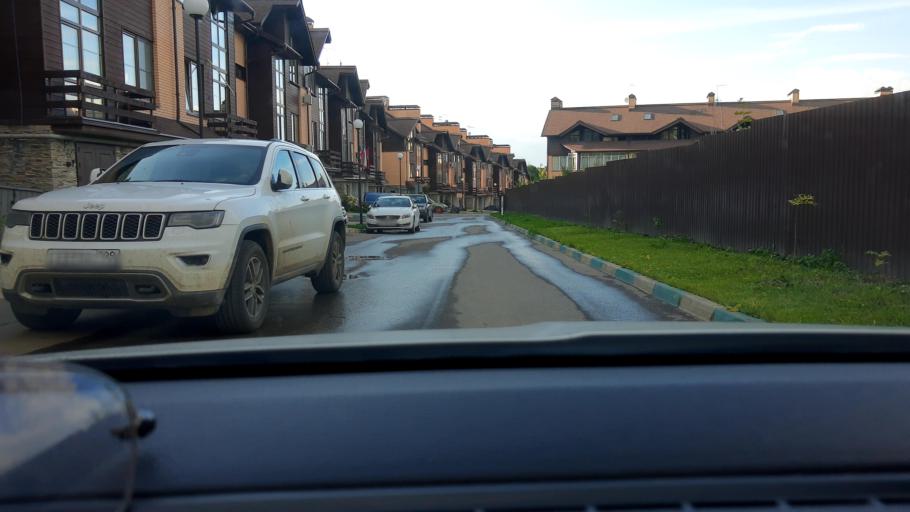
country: RU
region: Moskovskaya
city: Kommunarka
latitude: 55.5271
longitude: 37.4562
